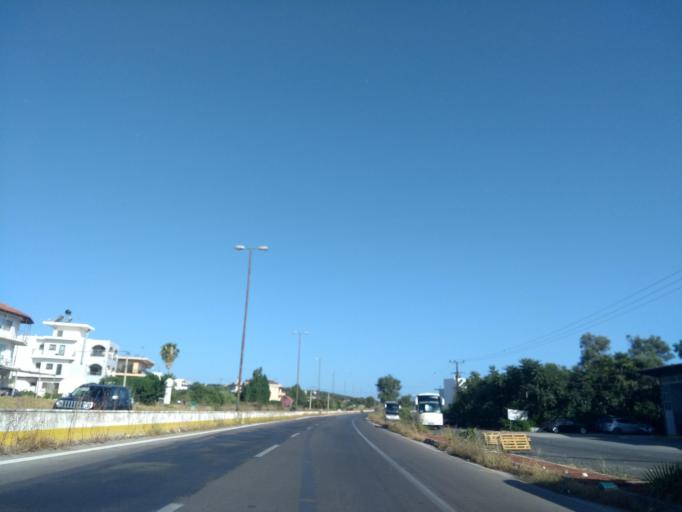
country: GR
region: Crete
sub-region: Nomos Chanias
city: Perivolia
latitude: 35.4951
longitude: 23.9986
